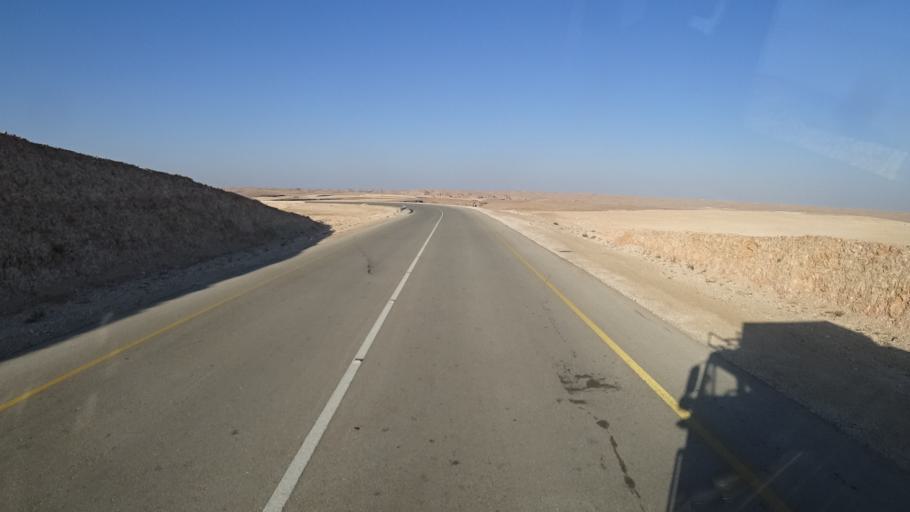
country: YE
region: Al Mahrah
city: Hawf
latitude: 17.0795
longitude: 53.0320
